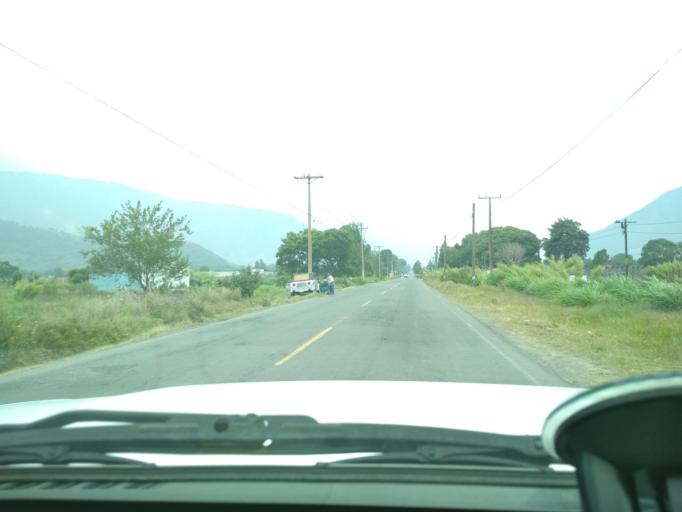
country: MX
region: Veracruz
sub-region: Nogales
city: Taza de Agua Ojo Zarco
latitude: 18.7751
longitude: -97.2125
